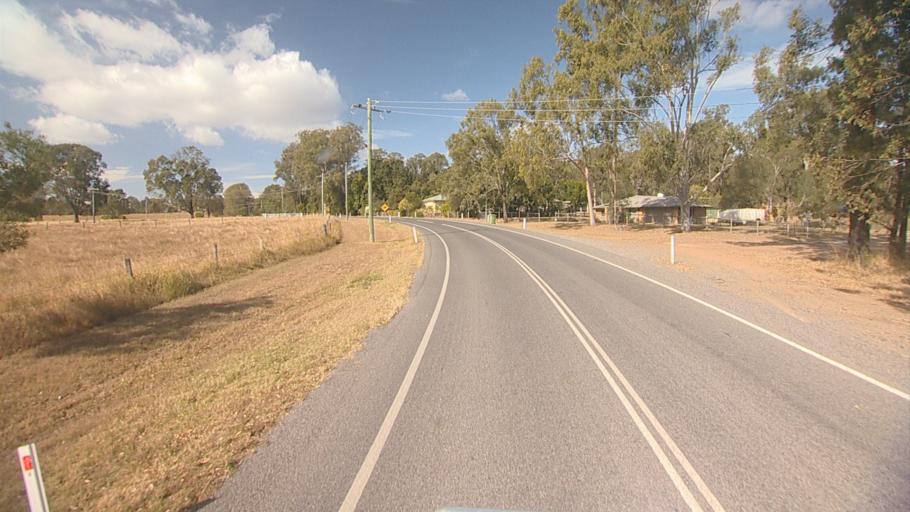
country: AU
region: Queensland
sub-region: Logan
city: Cedar Vale
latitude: -27.8662
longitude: 153.0090
